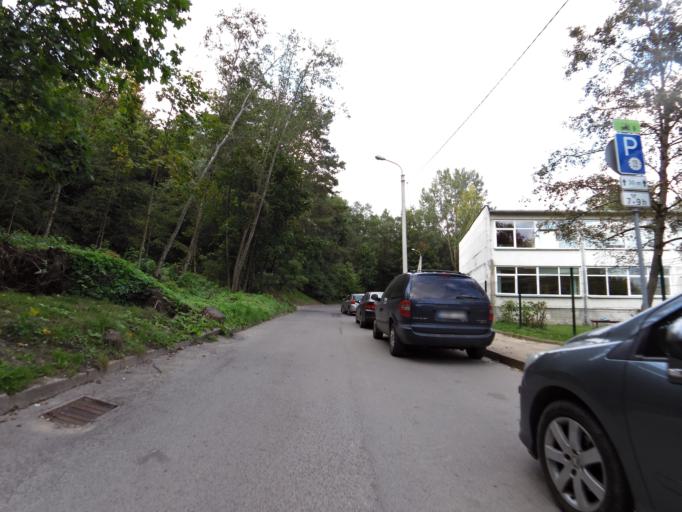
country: LT
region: Vilnius County
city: Seskine
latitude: 54.7045
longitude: 25.2491
